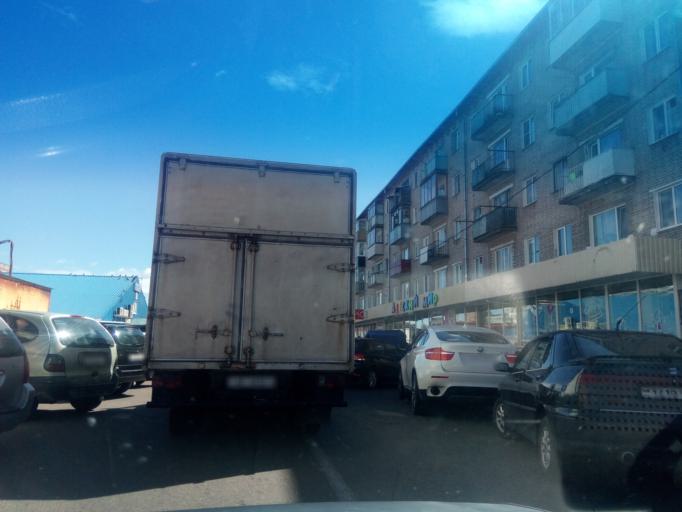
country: BY
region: Vitebsk
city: Polatsk
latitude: 55.4879
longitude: 28.7796
